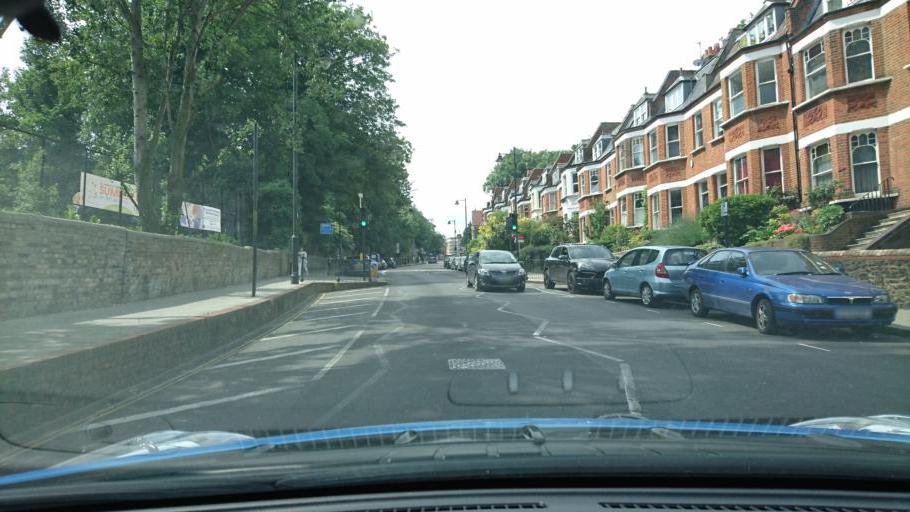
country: GB
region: England
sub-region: Greater London
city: Crouch End
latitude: 51.5681
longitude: -0.1397
